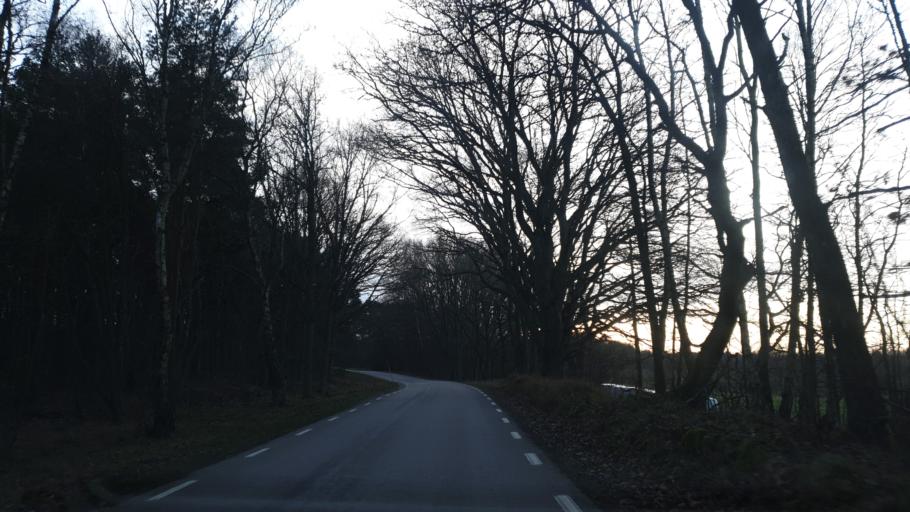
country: SE
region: Blekinge
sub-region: Karlskrona Kommun
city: Jaemjoe
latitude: 56.1456
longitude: 15.8972
